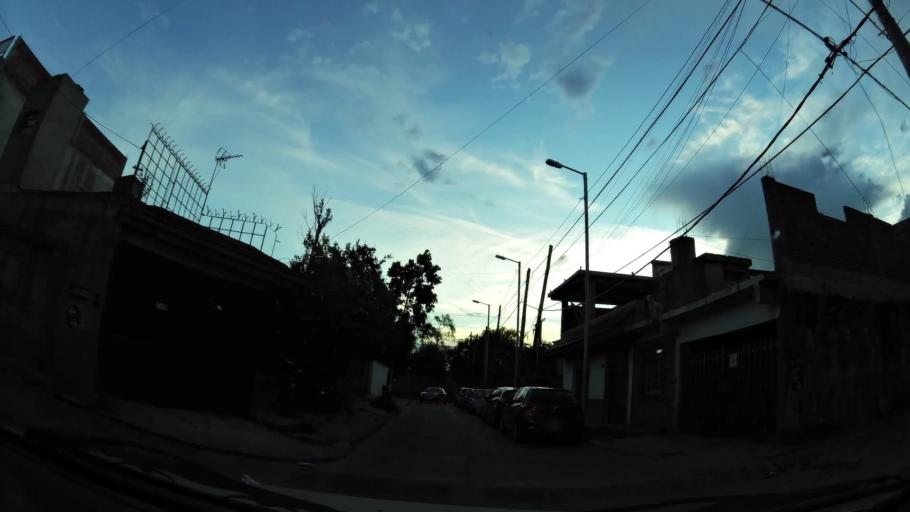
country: AR
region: Buenos Aires
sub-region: Partido de Avellaneda
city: Avellaneda
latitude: -34.6850
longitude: -58.3334
